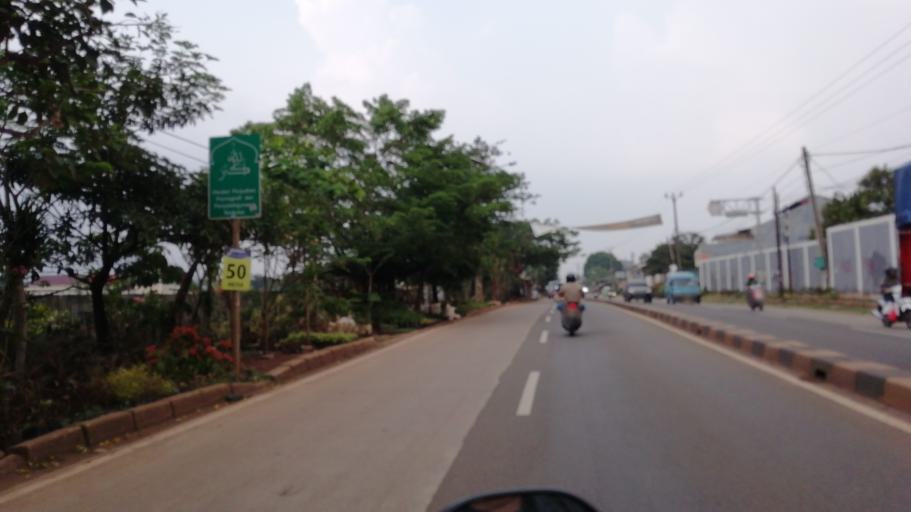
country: ID
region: West Java
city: Parung
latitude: -6.4628
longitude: 106.7298
